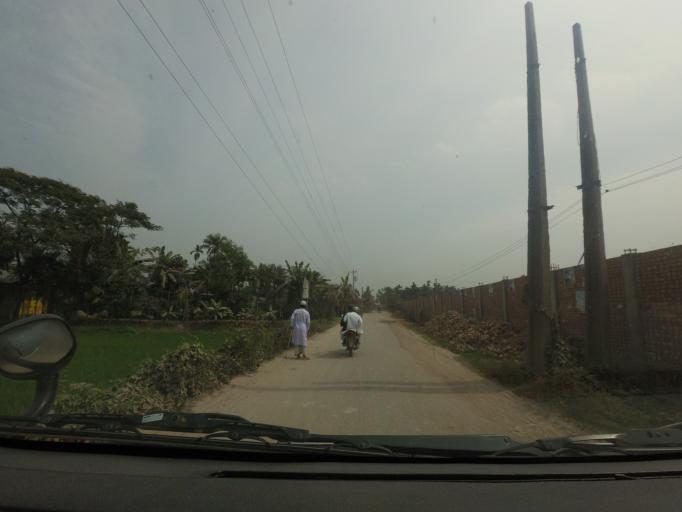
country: BD
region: Dhaka
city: Kishorganj
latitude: 24.3457
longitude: 90.7596
